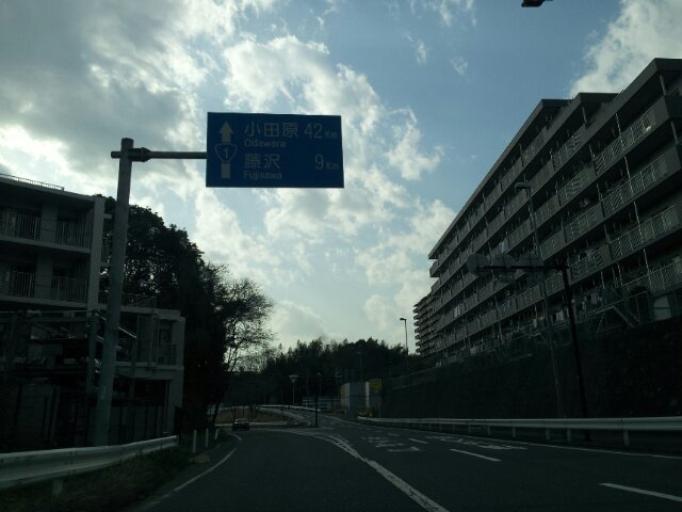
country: JP
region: Kanagawa
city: Fujisawa
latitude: 35.4136
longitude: 139.5389
